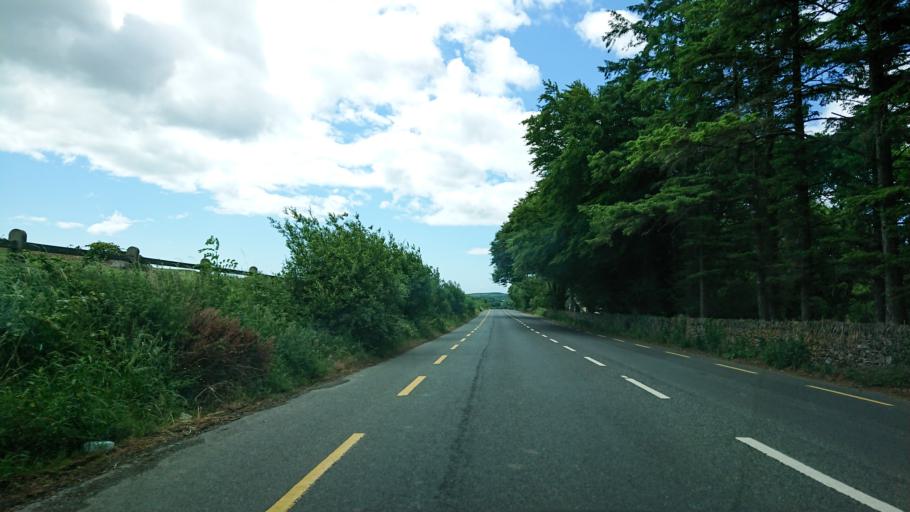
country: IE
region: Munster
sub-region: Waterford
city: Tra Mhor
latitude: 52.2045
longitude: -7.1953
